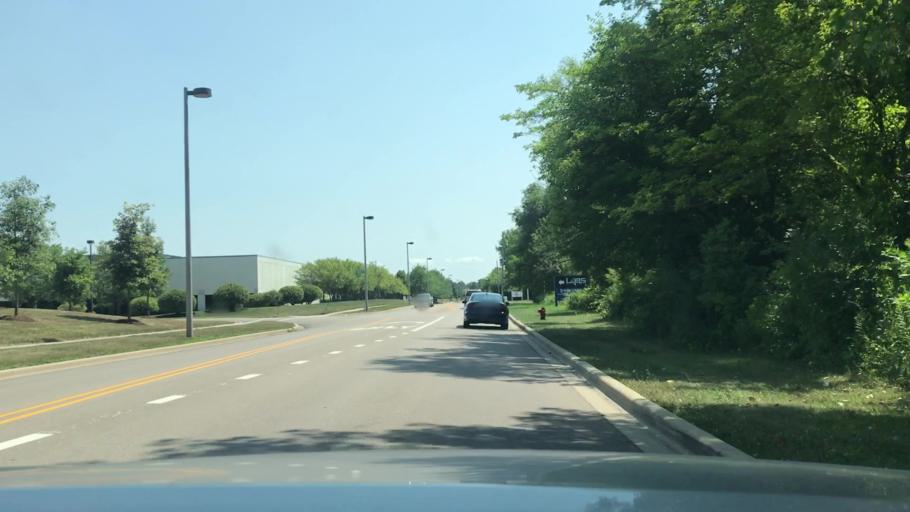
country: US
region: Illinois
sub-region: Kane County
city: Aurora
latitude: 41.7396
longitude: -88.2302
